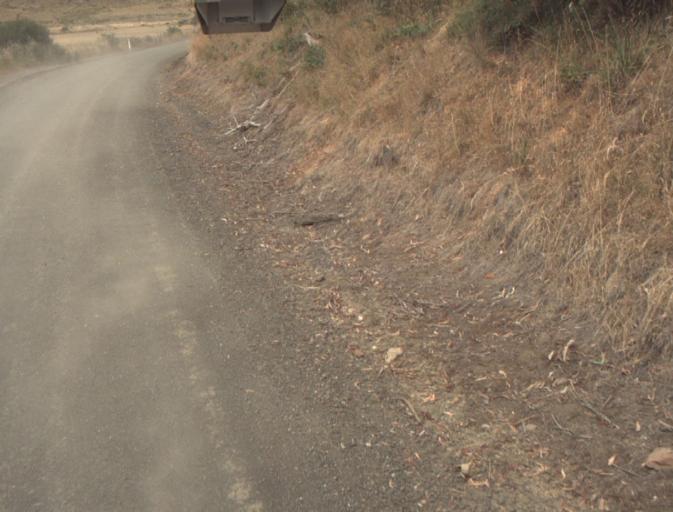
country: AU
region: Tasmania
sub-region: Northern Midlands
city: Evandale
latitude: -41.4903
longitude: 147.4355
